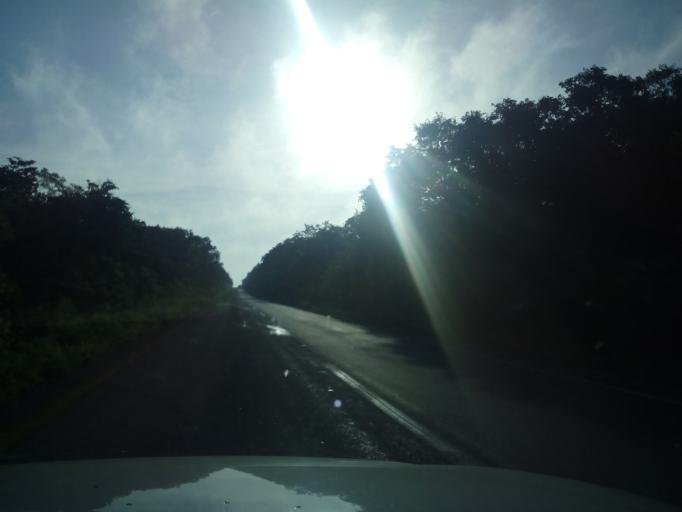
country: MX
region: Yucatan
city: Piste
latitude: 20.7478
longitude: -88.7073
